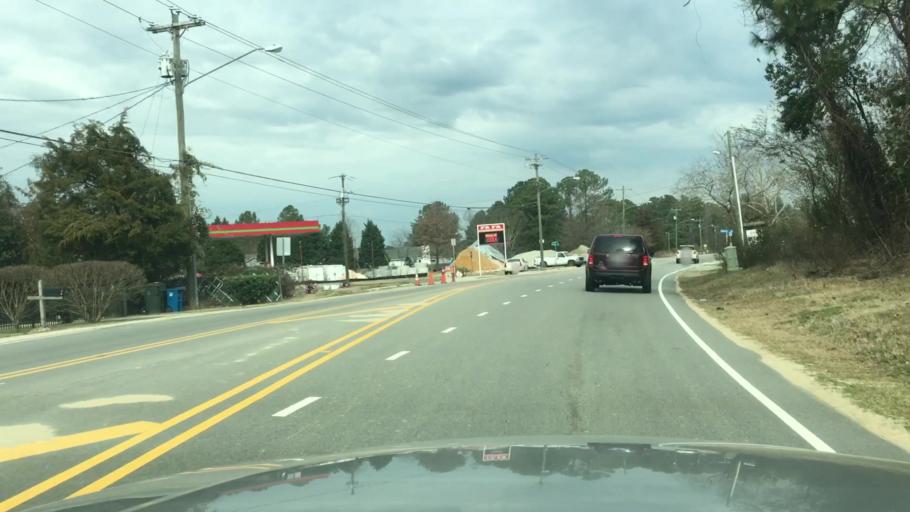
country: US
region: North Carolina
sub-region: Hoke County
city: Rockfish
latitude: 35.0241
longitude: -79.0024
